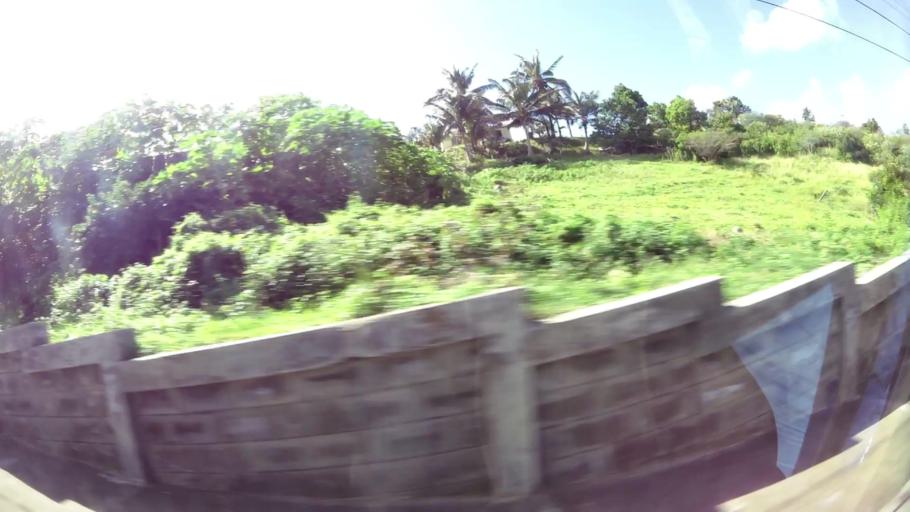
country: MS
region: Saint Peter
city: Brades
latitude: 16.7869
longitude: -62.2090
